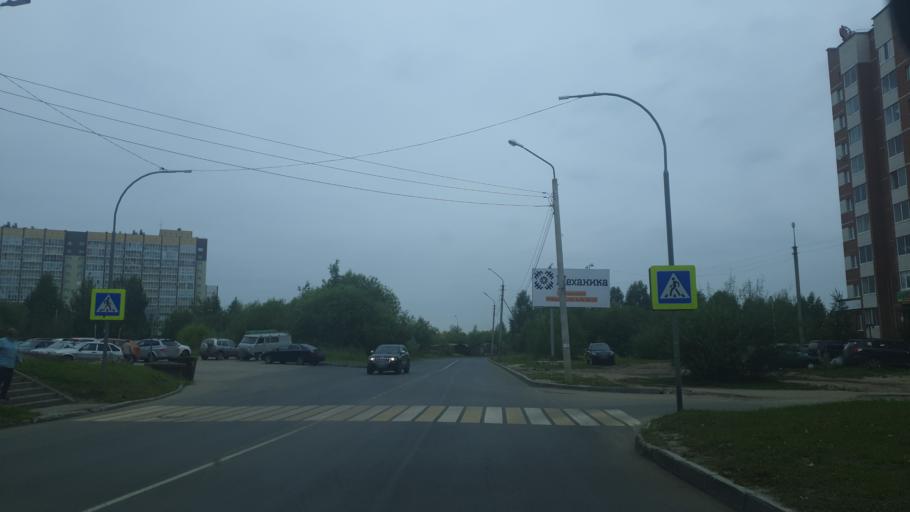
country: RU
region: Komi Republic
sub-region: Syktyvdinskiy Rayon
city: Syktyvkar
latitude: 61.6947
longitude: 50.8094
